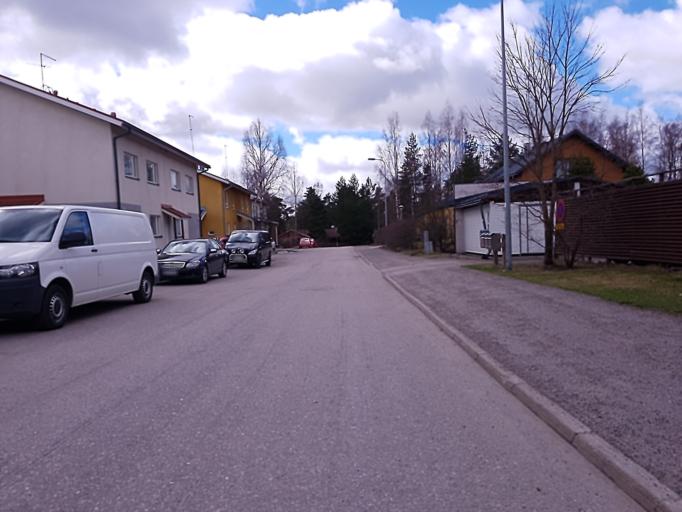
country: FI
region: Uusimaa
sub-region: Helsinki
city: Helsinki
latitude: 60.2410
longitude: 24.9005
